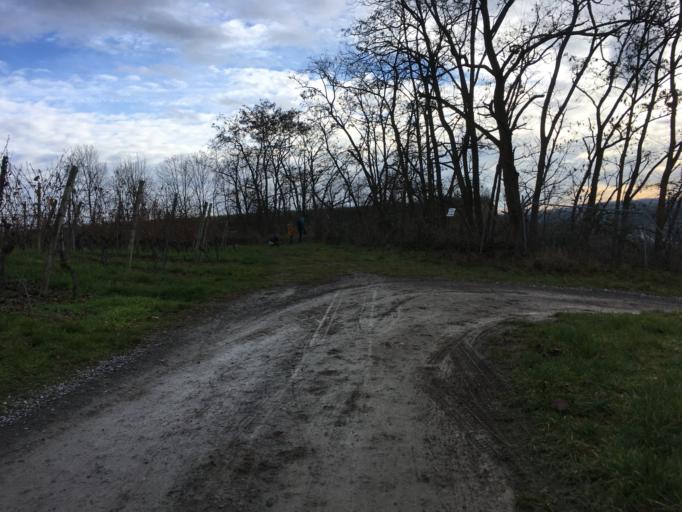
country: DE
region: Baden-Wuerttemberg
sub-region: Regierungsbezirk Stuttgart
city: Ilsfeld
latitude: 49.0603
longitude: 9.2170
